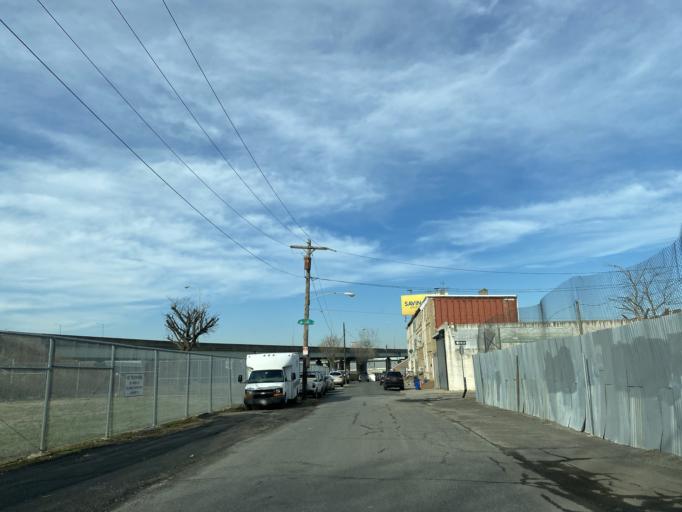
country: US
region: New Jersey
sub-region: Camden County
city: Pennsauken
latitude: 39.9951
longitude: -75.0792
